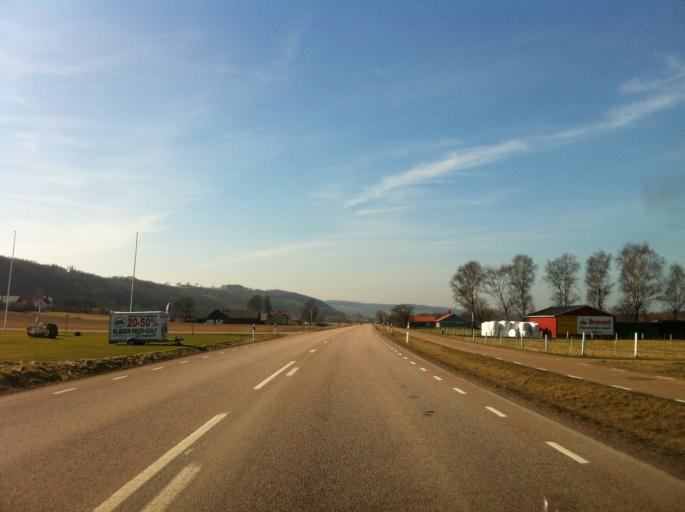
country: SE
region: Skane
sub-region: Bastads Kommun
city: Bastad
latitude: 56.4284
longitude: 12.9150
